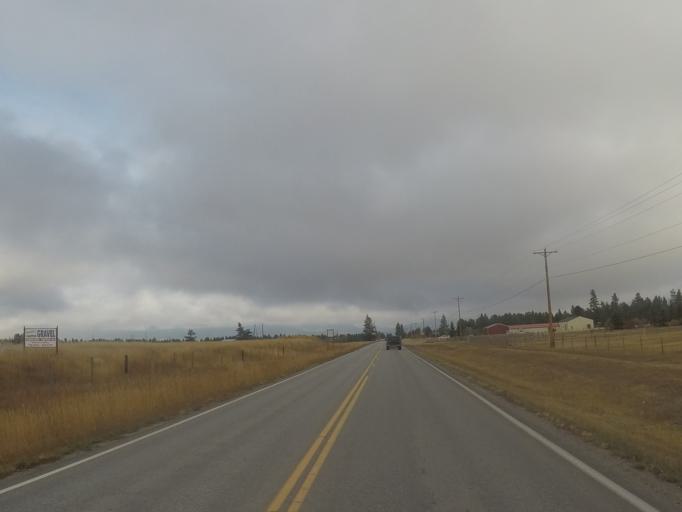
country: US
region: Montana
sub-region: Flathead County
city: Columbia Falls
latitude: 48.3456
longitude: -114.1593
